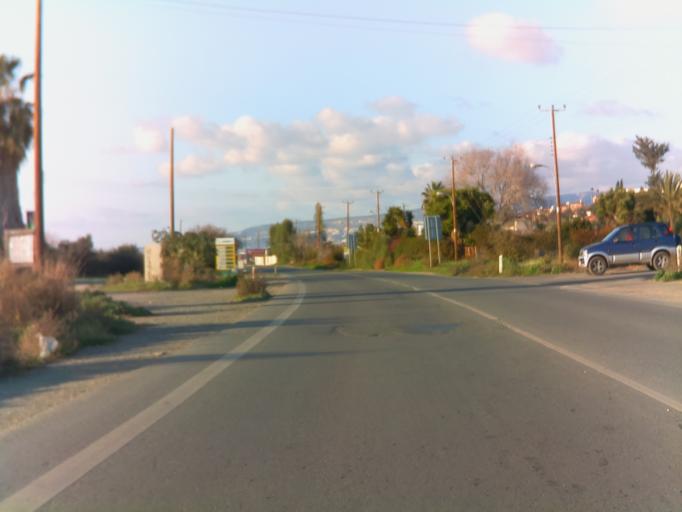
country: CY
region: Pafos
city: Chlorakas
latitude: 34.7983
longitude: 32.4007
